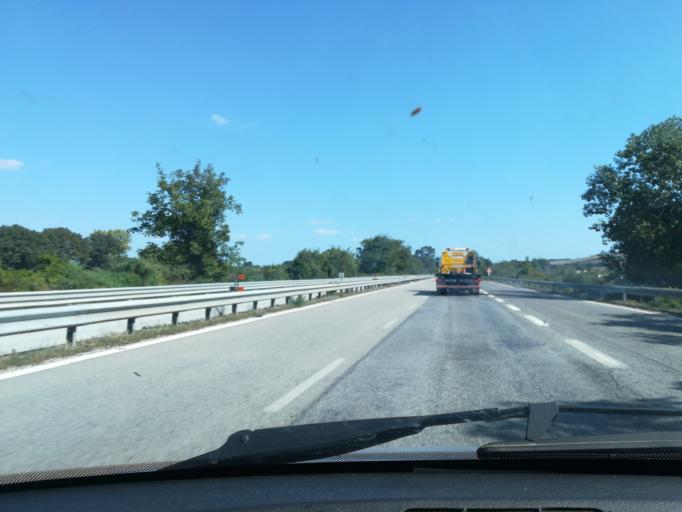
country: IT
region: The Marches
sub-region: Provincia di Macerata
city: Casette Verdini
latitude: 43.2342
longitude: 13.3723
